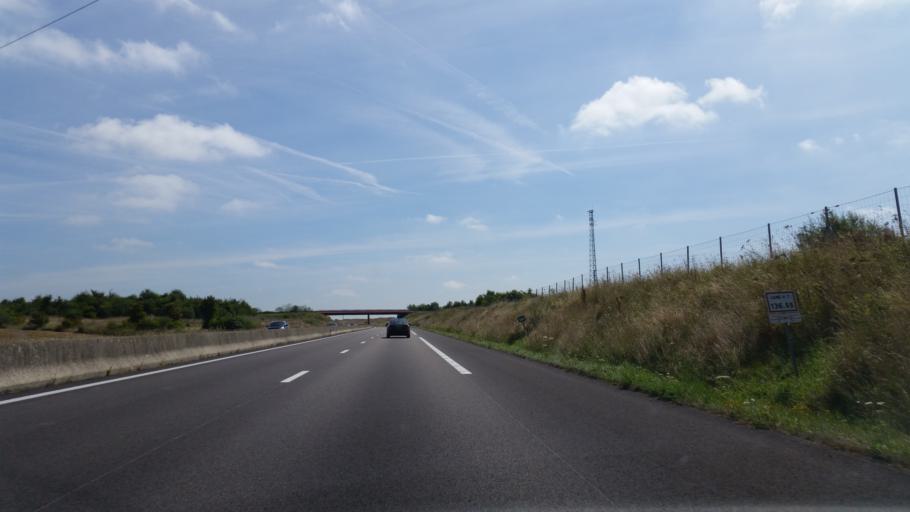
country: FR
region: Haute-Normandie
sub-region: Departement de la Seine-Maritime
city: Gaillefontaine
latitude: 49.7397
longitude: 1.6058
